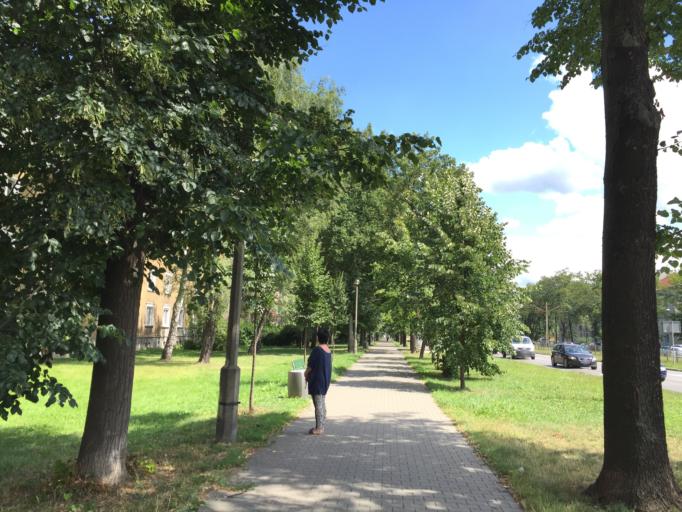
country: PL
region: Lesser Poland Voivodeship
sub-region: Powiat wielicki
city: Kokotow
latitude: 50.0699
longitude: 20.0462
